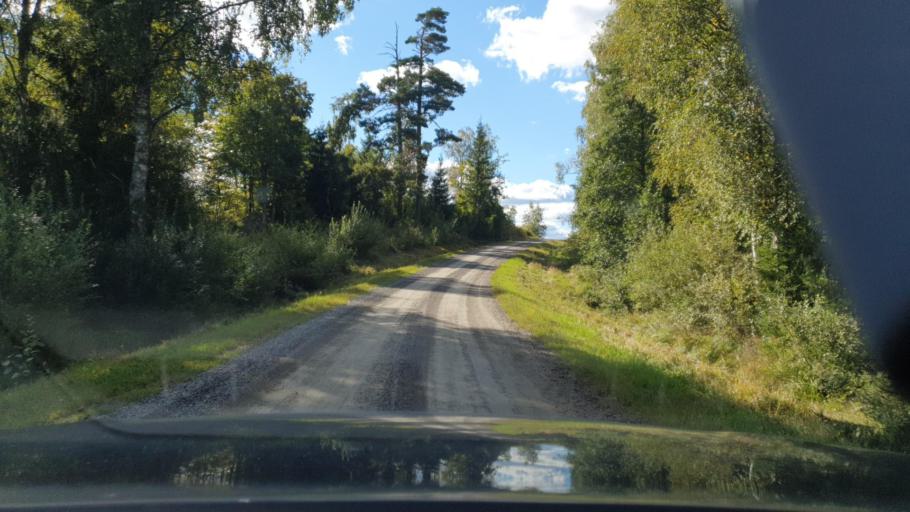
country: SE
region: Vaermland
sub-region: Filipstads Kommun
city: Filipstad
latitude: 59.7840
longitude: 14.0871
